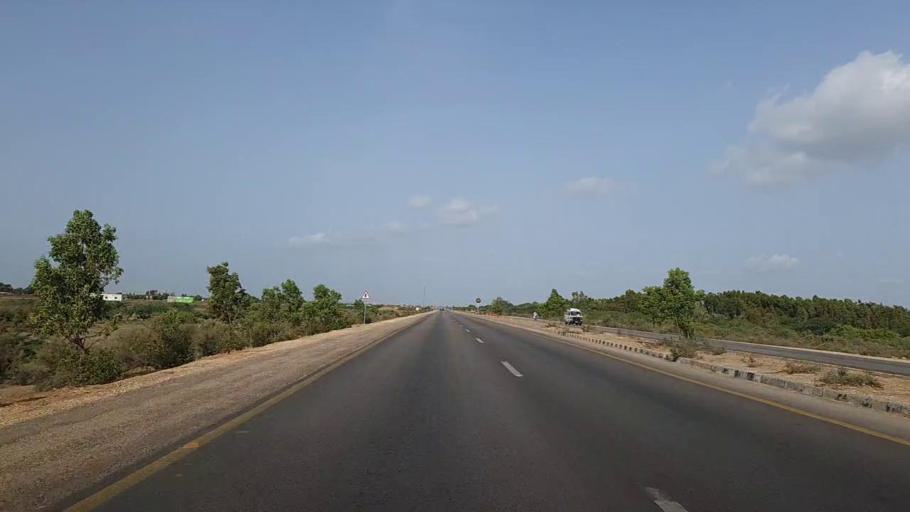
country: PK
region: Sindh
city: Gharo
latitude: 24.7391
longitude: 67.7372
